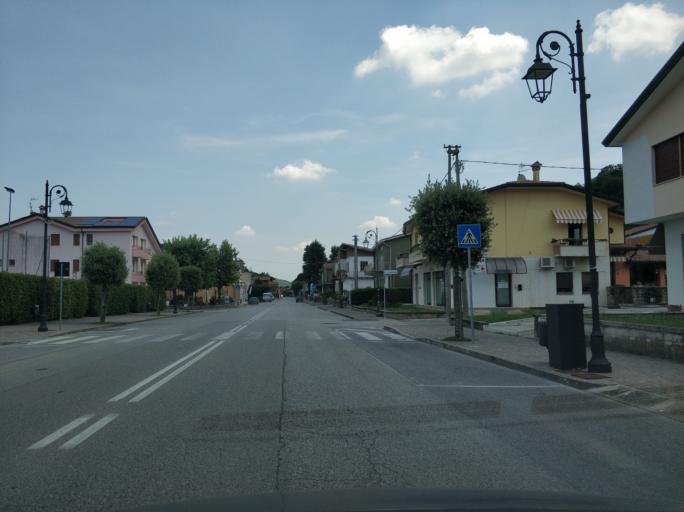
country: IT
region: Veneto
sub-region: Provincia di Padova
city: Galzignano
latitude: 45.3079
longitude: 11.7303
